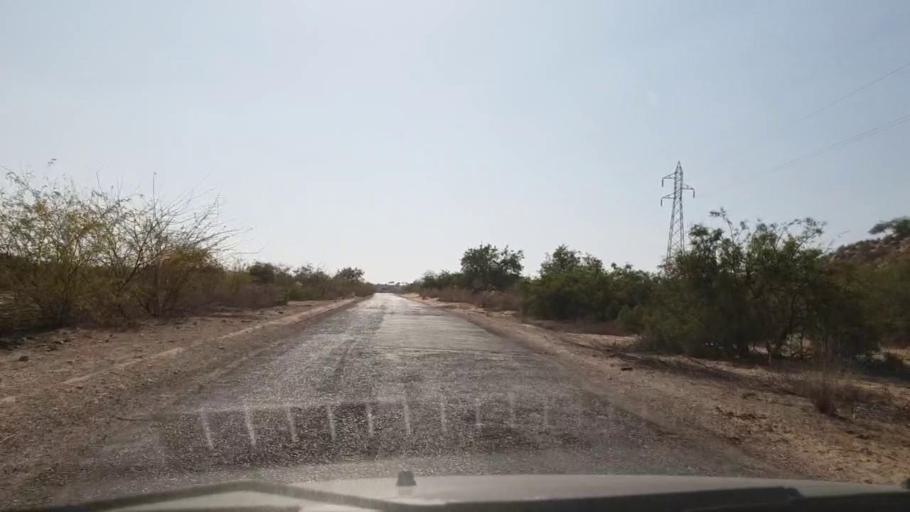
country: PK
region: Sindh
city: Mithi
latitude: 24.6386
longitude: 69.7434
